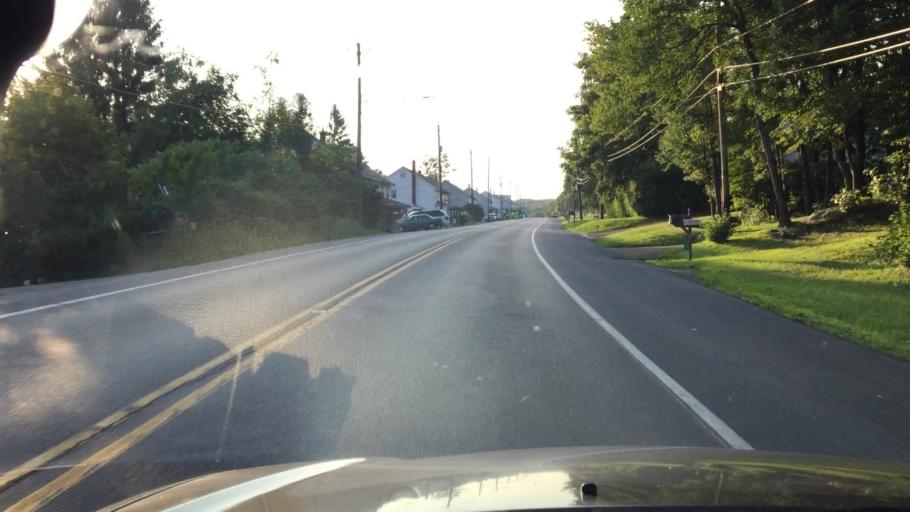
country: US
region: Pennsylvania
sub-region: Luzerne County
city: Hazleton
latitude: 40.9326
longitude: -75.9236
